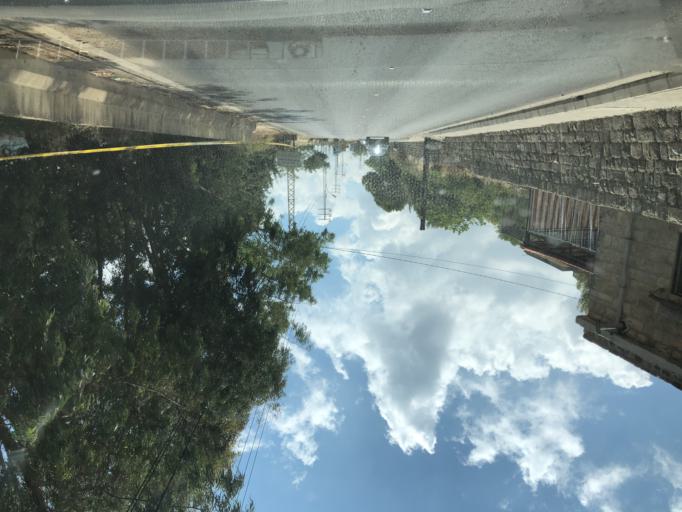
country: LB
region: Mont-Liban
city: Beit ed Dine
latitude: 33.6987
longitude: 35.5955
